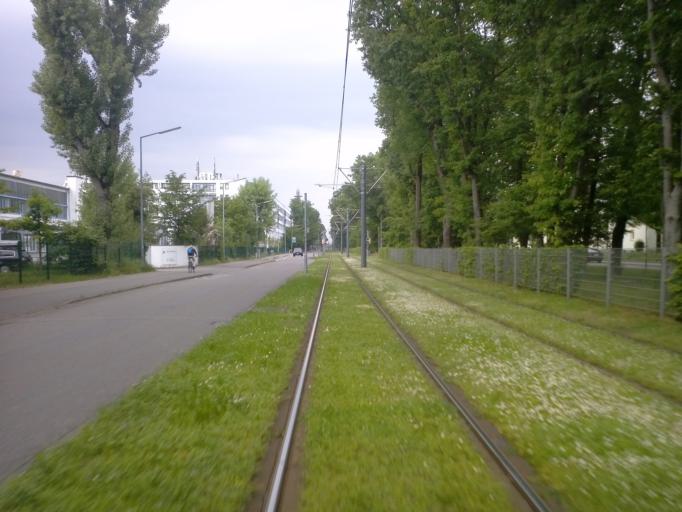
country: DE
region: Baden-Wuerttemberg
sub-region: Karlsruhe Region
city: Karlsruhe
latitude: 49.0236
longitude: 8.3858
